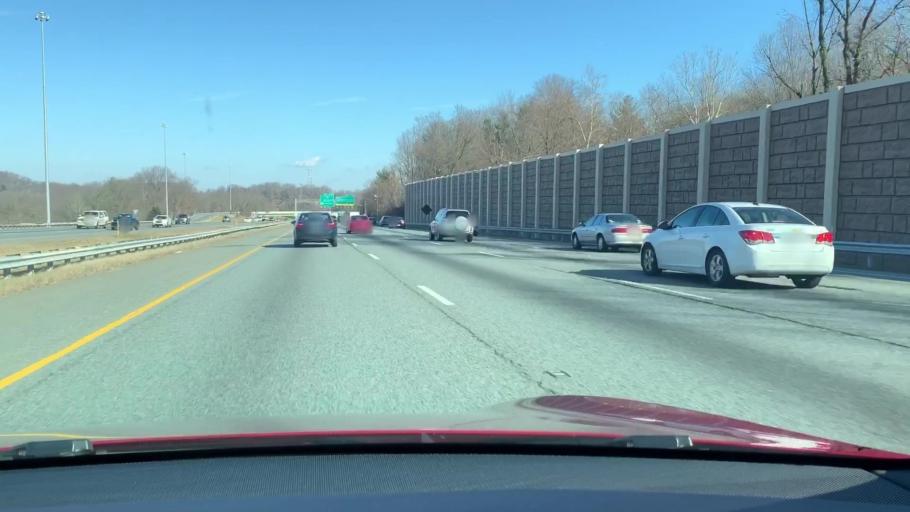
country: US
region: Maryland
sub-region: Howard County
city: West Elkridge
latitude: 39.2210
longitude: -76.7252
